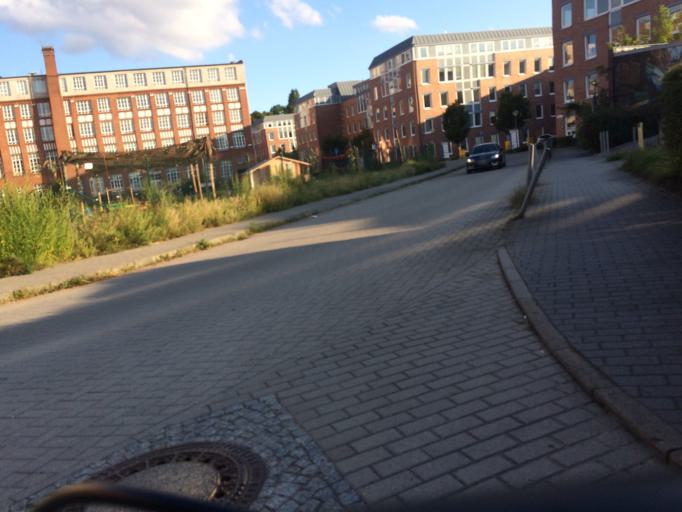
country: DE
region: Berlin
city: Heinersdorf
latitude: 52.5581
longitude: 13.4406
